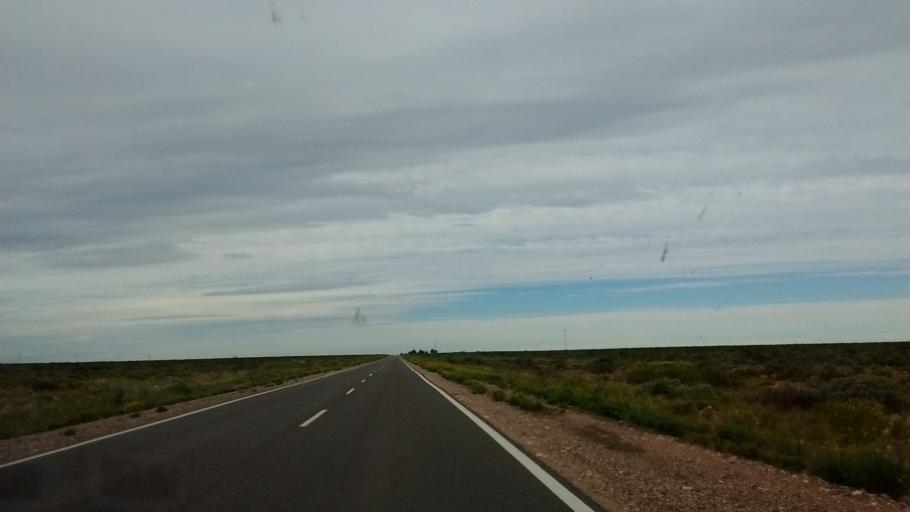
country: AR
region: Rio Negro
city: Contraalmirante Cordero
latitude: -38.3803
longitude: -68.0236
